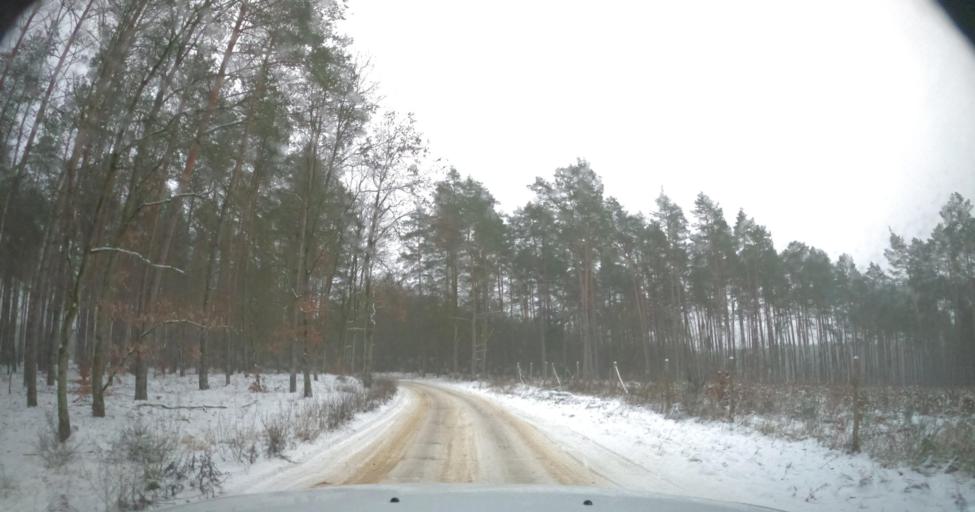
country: PL
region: West Pomeranian Voivodeship
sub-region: Powiat kamienski
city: Golczewo
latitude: 53.8399
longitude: 14.9983
